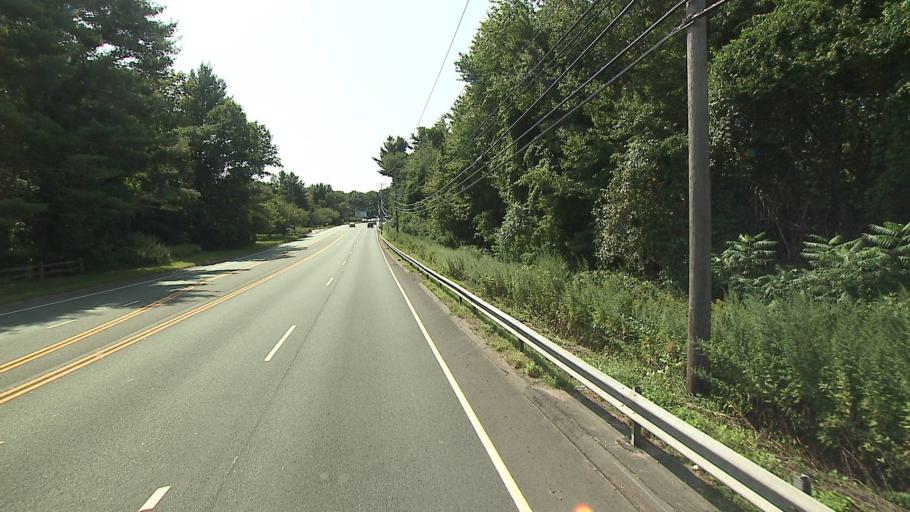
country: US
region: Connecticut
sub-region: Fairfield County
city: Newtown
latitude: 41.3704
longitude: -73.2716
